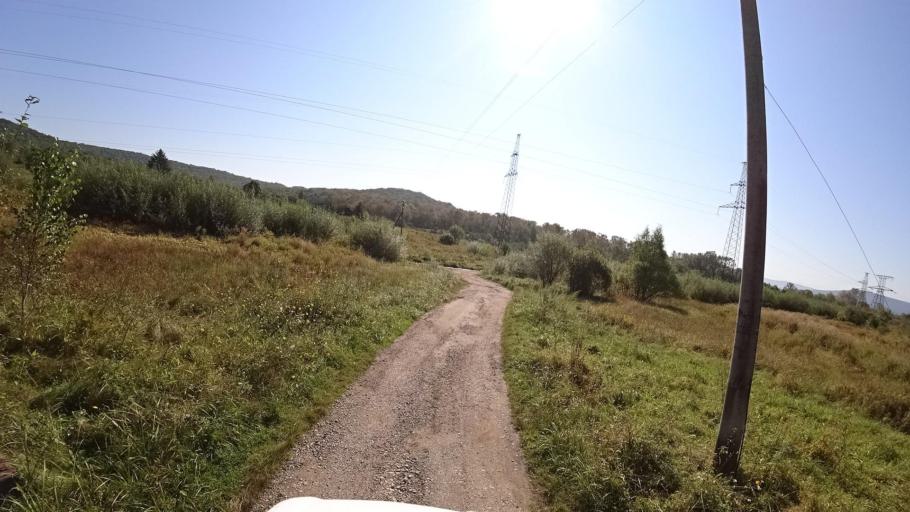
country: RU
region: Jewish Autonomous Oblast
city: Bira
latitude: 49.0016
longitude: 132.4761
